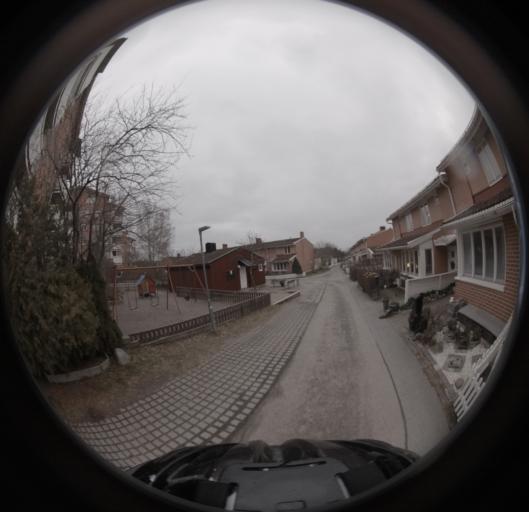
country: SE
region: Stockholm
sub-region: Upplands Vasby Kommun
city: Upplands Vaesby
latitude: 59.4838
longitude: 17.9280
